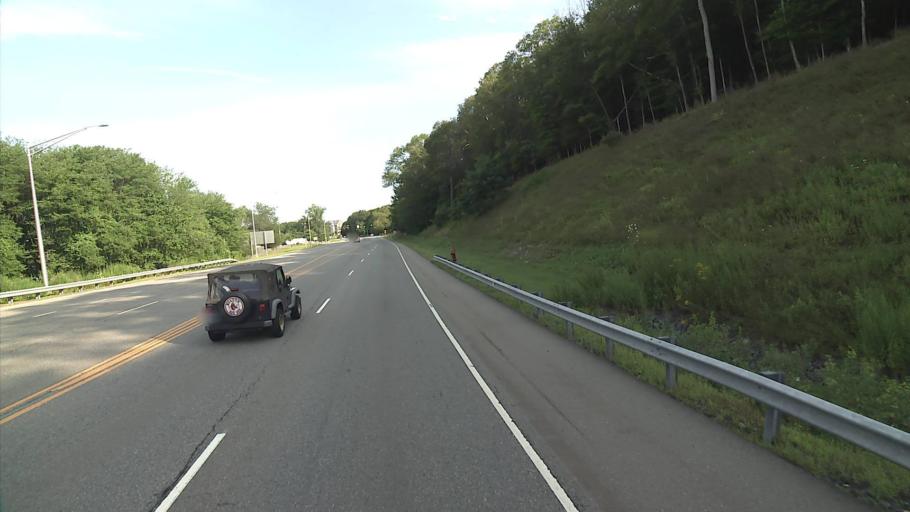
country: US
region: Connecticut
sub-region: New London County
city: Preston City
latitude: 41.4833
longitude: -71.9689
